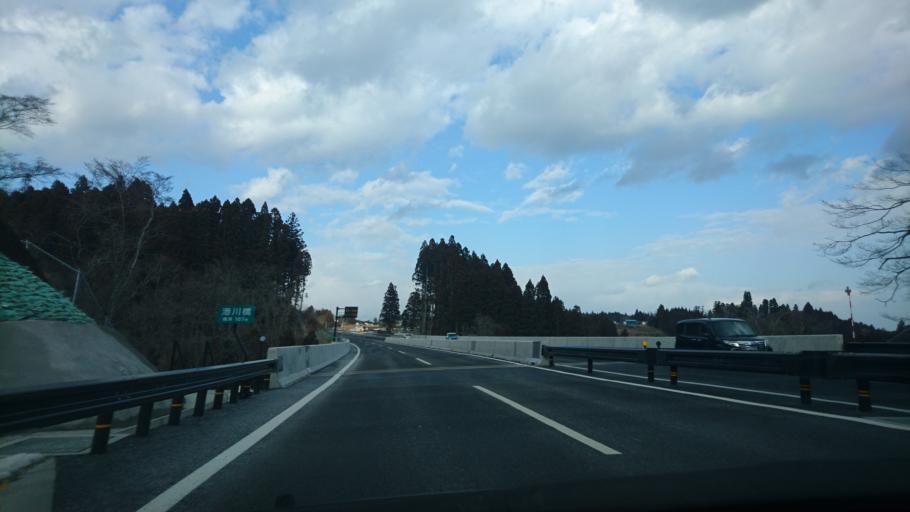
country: JP
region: Miyagi
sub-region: Oshika Gun
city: Onagawa Cho
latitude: 38.7369
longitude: 141.5225
